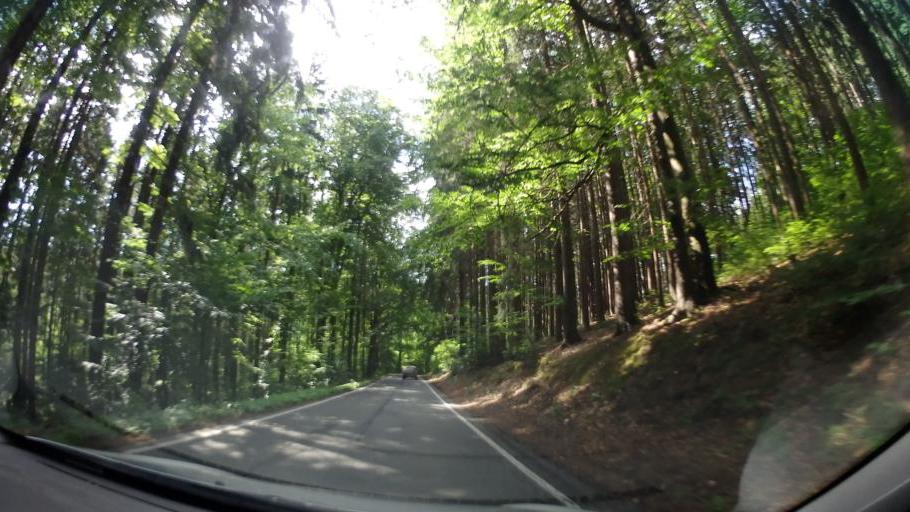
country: CZ
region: Olomoucky
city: Zabreh
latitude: 49.8607
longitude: 16.8287
